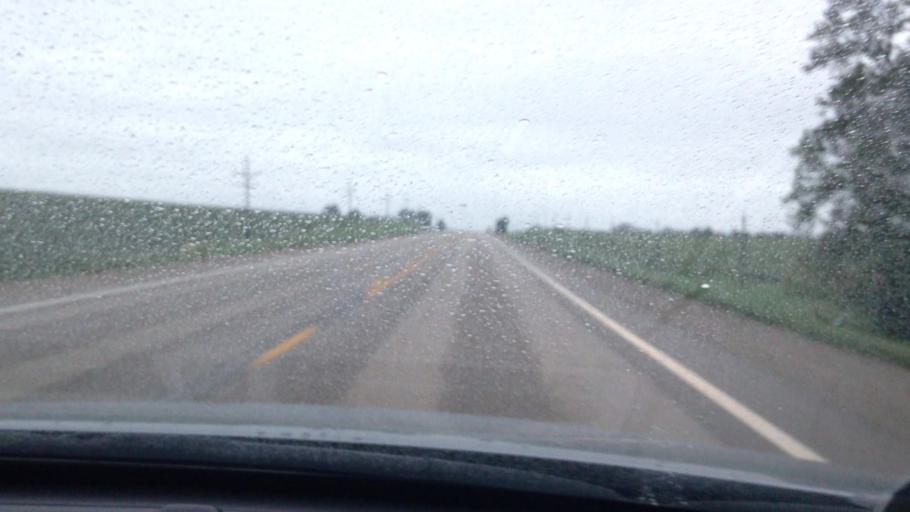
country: US
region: Kansas
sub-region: Brown County
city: Hiawatha
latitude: 39.8109
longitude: -95.5273
